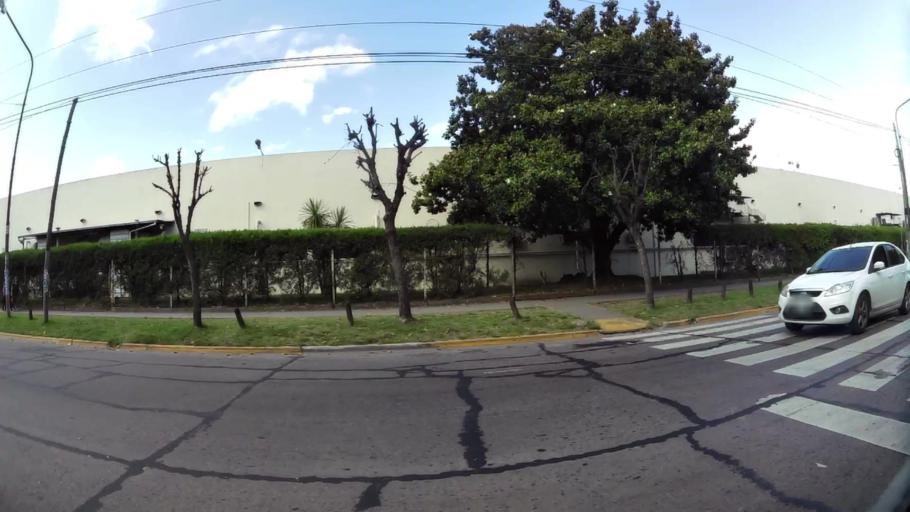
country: AR
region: Buenos Aires
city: San Justo
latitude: -34.6706
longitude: -58.5646
